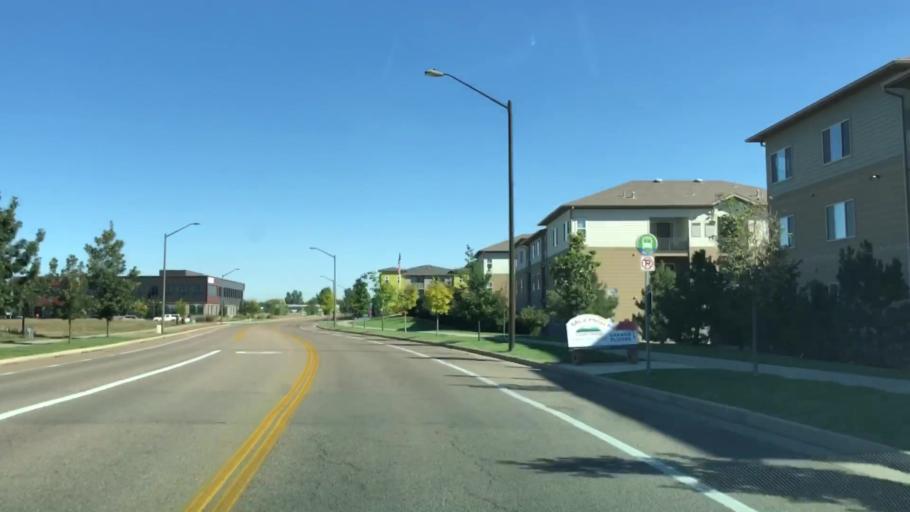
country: US
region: Colorado
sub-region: Larimer County
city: Fort Collins
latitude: 40.5163
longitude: -105.0105
